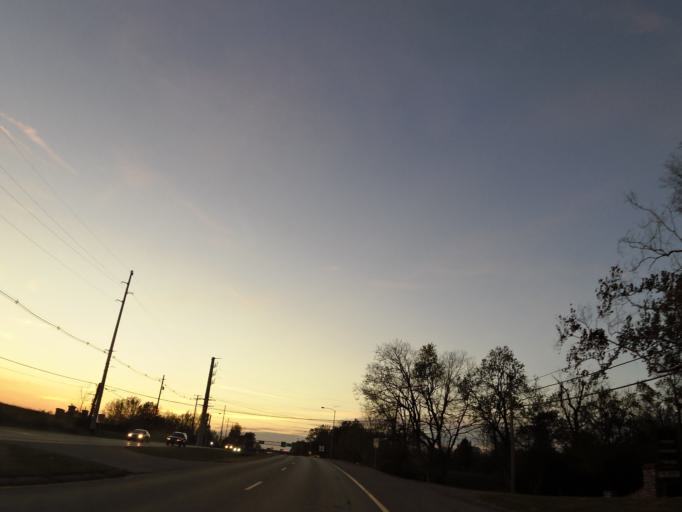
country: US
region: Kentucky
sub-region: Fayette County
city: Lexington-Fayette
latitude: 38.0406
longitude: -84.4134
